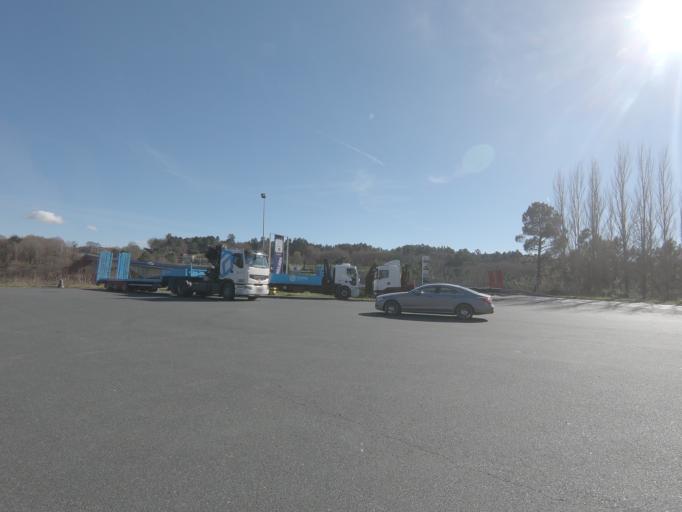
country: ES
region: Galicia
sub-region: Provincia de Pontevedra
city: Silleda
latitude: 42.6860
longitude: -8.2014
